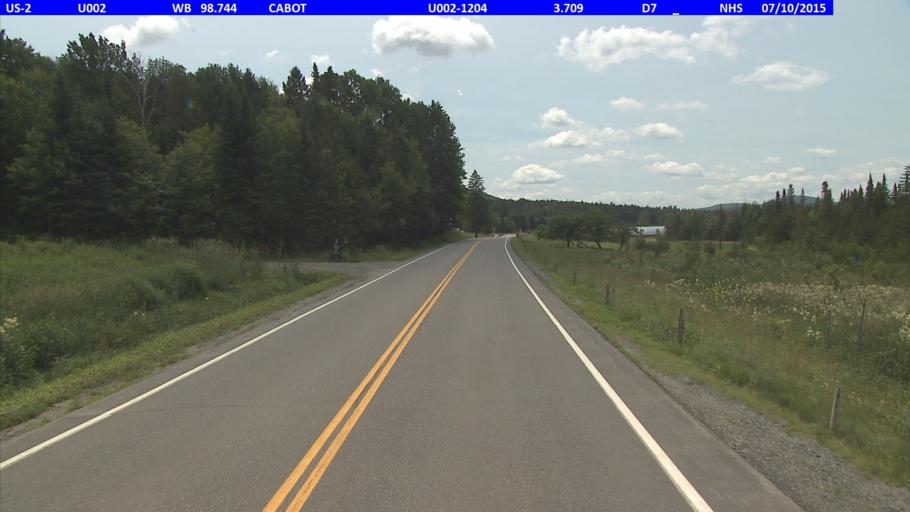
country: US
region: Vermont
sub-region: Caledonia County
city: Hardwick
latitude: 44.3781
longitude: -72.2592
